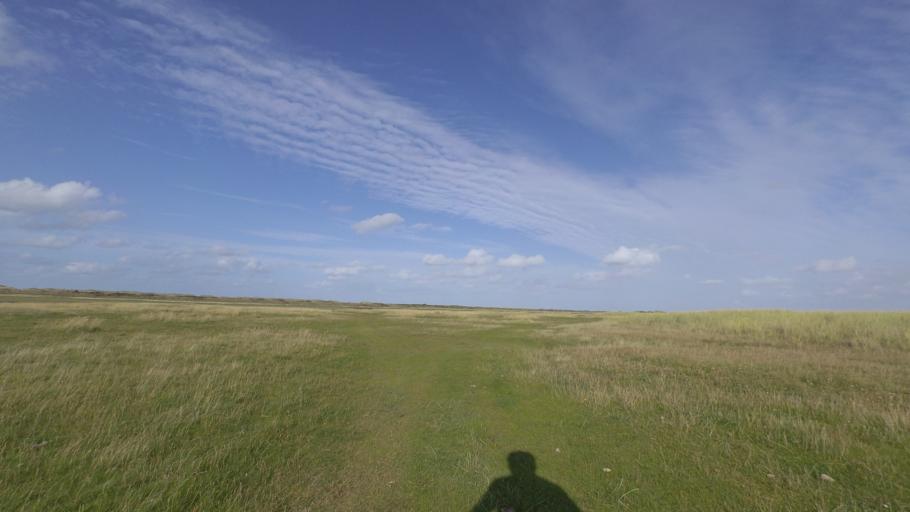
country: NL
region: Friesland
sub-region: Gemeente Ameland
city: Nes
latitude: 53.4553
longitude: 5.8644
